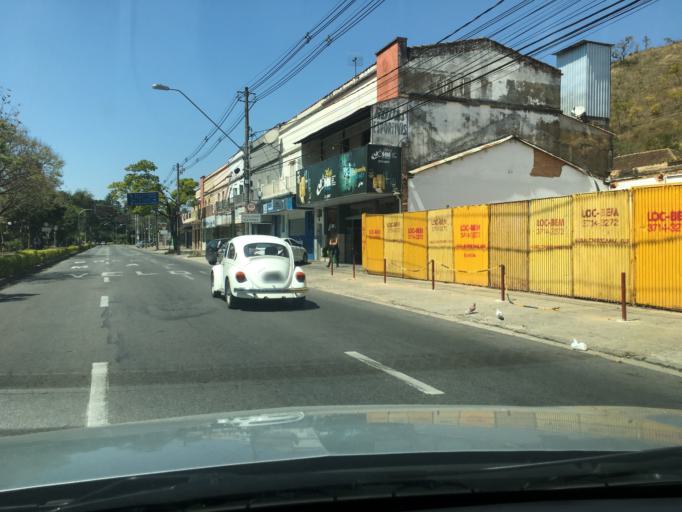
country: BR
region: Minas Gerais
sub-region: Pocos De Caldas
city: Pocos de Caldas
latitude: -21.7860
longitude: -46.5745
